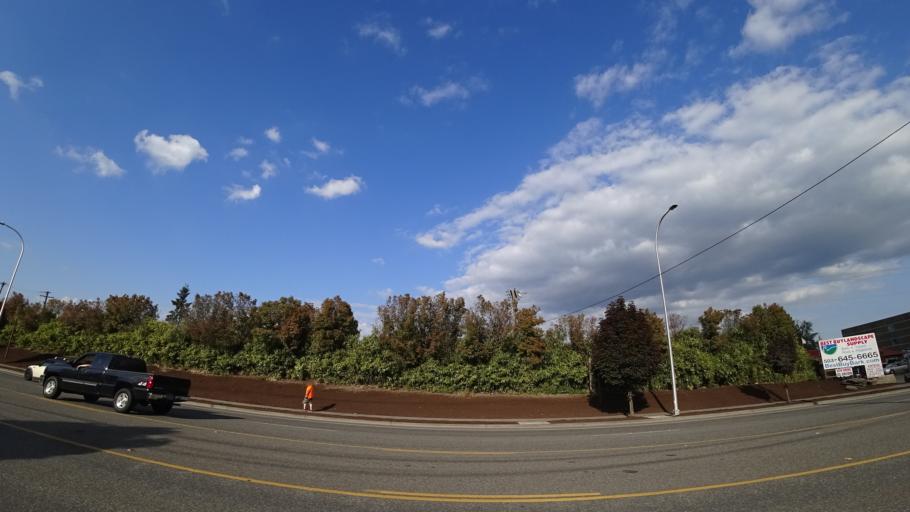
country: US
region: Oregon
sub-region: Washington County
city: Rockcreek
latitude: 45.5364
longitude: -122.9002
